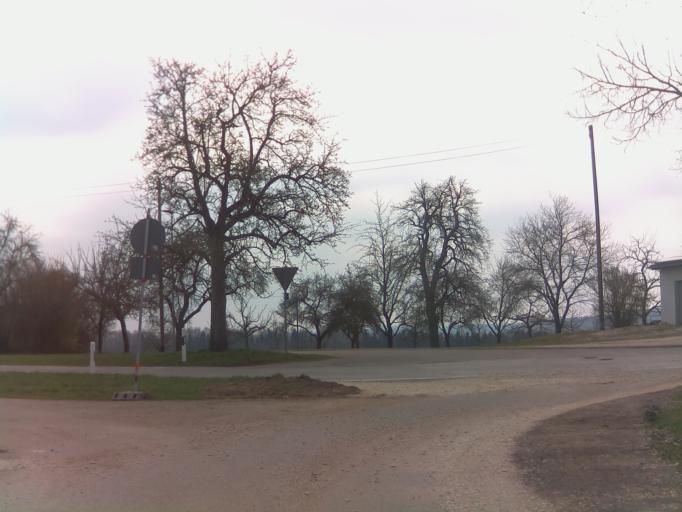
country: DE
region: Baden-Wuerttemberg
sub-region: Tuebingen Region
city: Mehrstetten
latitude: 48.4066
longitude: 9.5952
